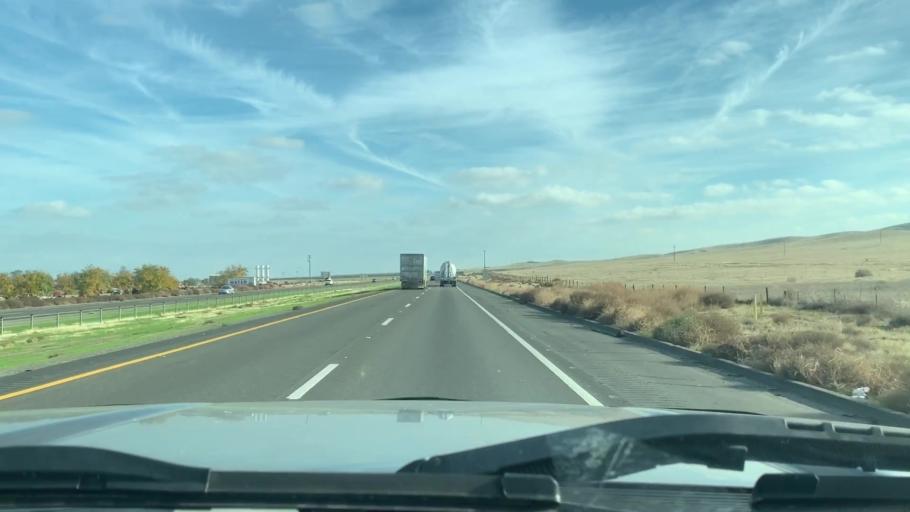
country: US
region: California
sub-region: Kings County
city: Avenal
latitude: 36.0729
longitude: -120.0959
